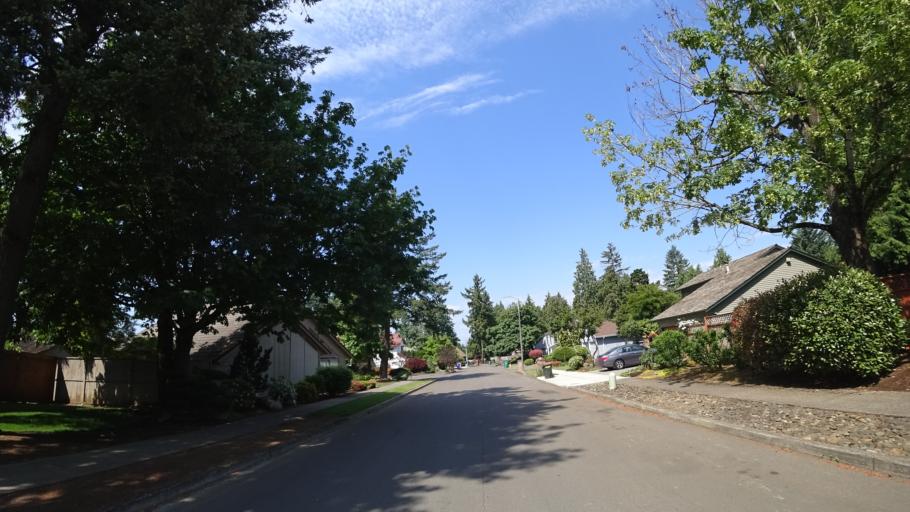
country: US
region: Oregon
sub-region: Multnomah County
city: Fairview
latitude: 45.5372
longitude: -122.4946
